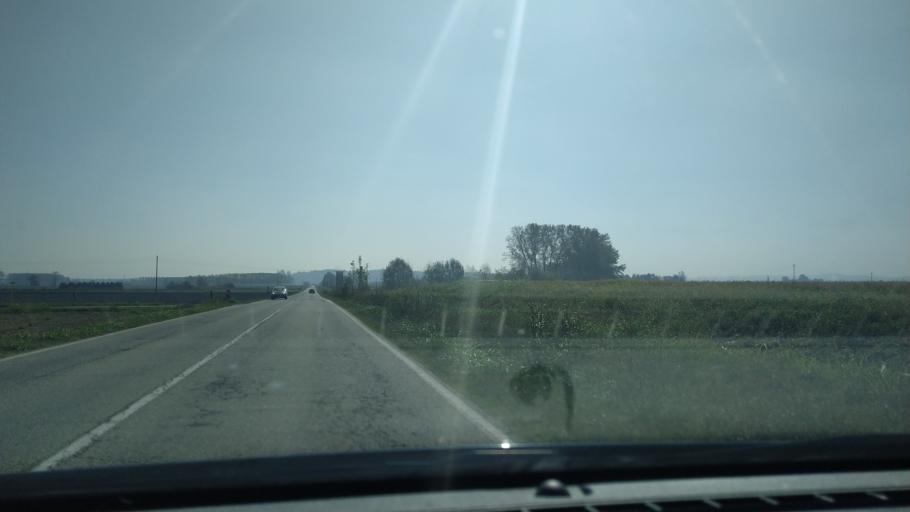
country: IT
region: Piedmont
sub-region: Provincia di Alessandria
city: Ticineto
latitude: 45.0823
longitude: 8.5604
